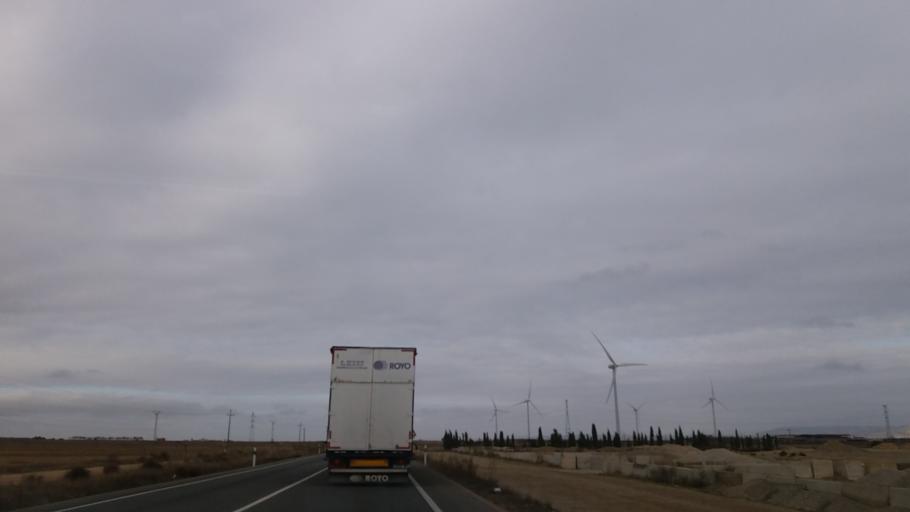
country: ES
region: Aragon
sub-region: Provincia de Zaragoza
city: Mallen
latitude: 41.8728
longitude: -1.3921
